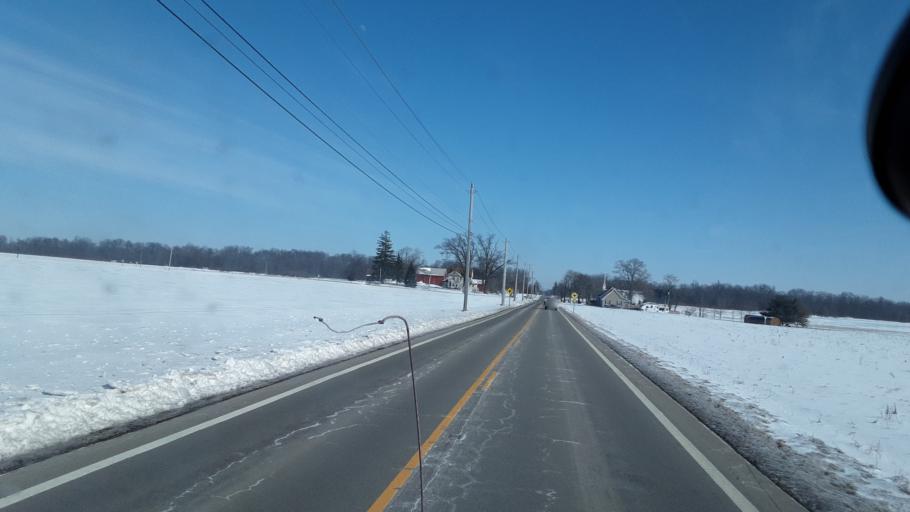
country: US
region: Ohio
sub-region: Columbiana County
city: Leetonia
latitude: 40.9438
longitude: -80.7677
